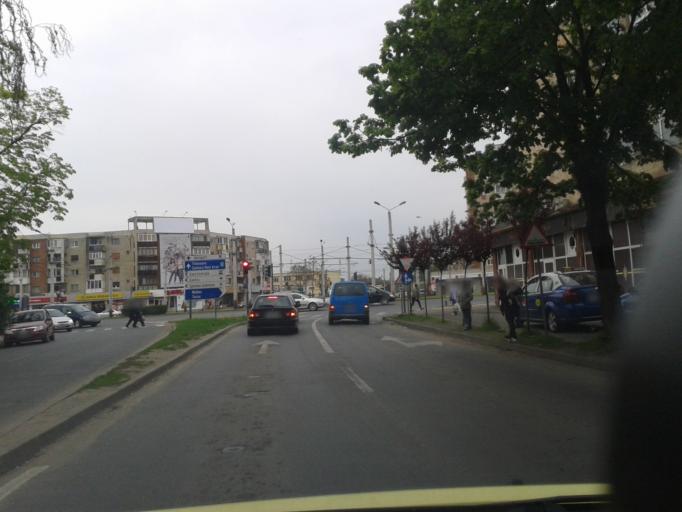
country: RO
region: Arad
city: Arad
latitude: 46.1931
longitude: 21.3082
